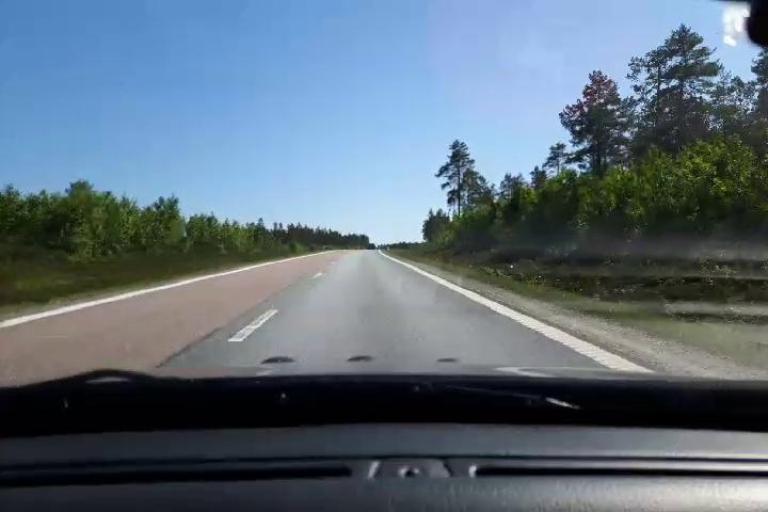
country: SE
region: Gaevleborg
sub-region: Soderhamns Kommun
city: Soderhamn
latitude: 61.3930
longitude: 16.9922
